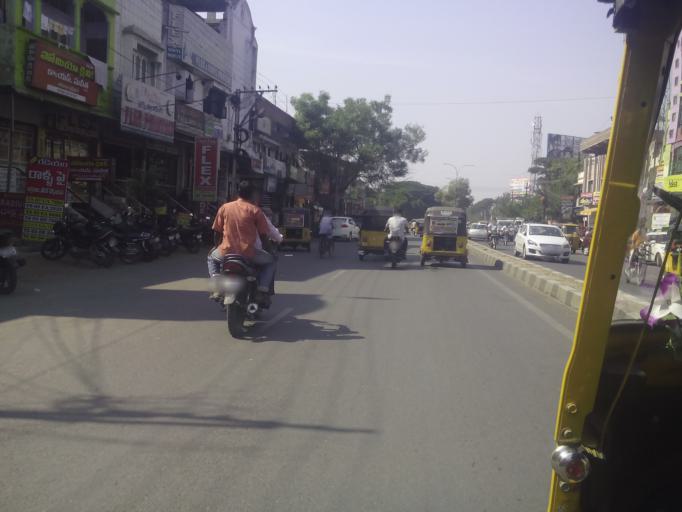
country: IN
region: Telangana
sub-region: Warangal
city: Warangal
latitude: 17.9900
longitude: 79.5957
